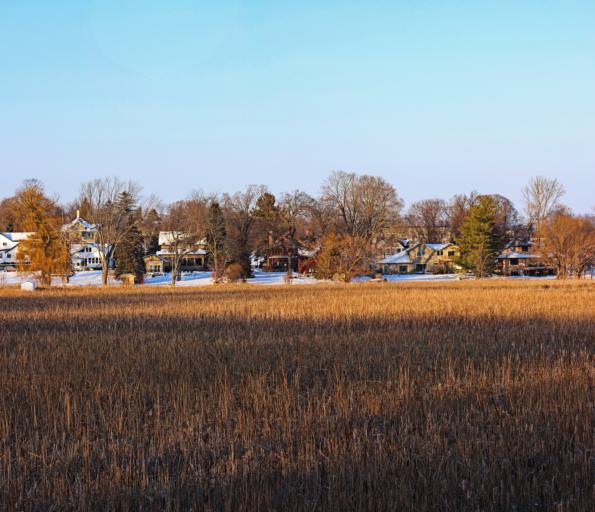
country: US
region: Wisconsin
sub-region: Jefferson County
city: Lake Mills
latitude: 43.0753
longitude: -88.9161
